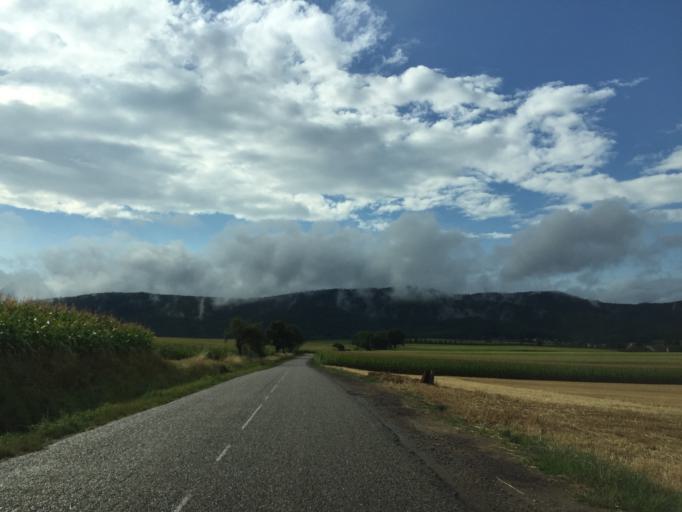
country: FR
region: Alsace
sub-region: Departement du Bas-Rhin
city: Soultz-sous-Forets
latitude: 48.9922
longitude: 7.8985
